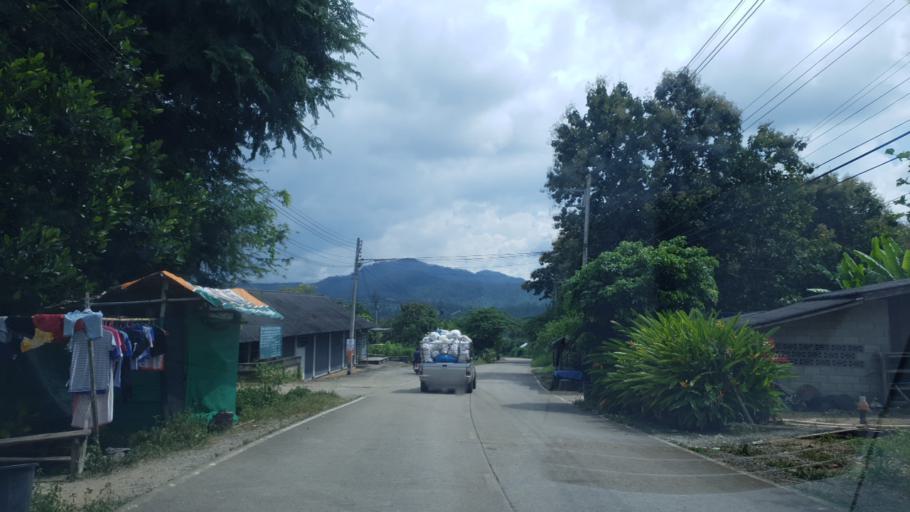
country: TH
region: Mae Hong Son
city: Khun Yuam
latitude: 18.8182
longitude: 97.9320
